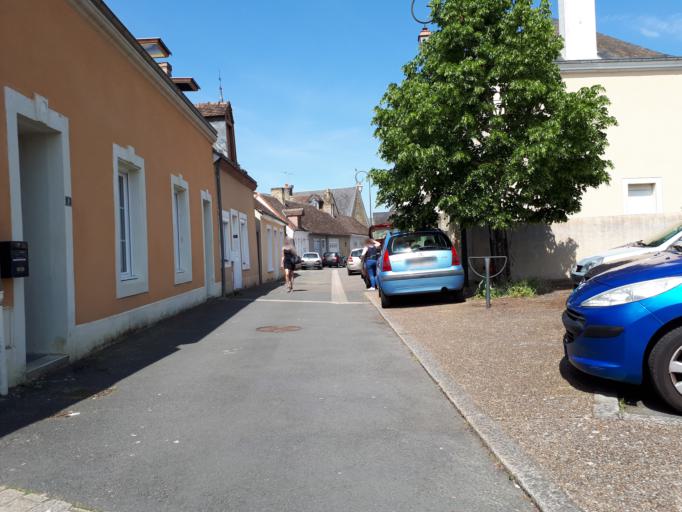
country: FR
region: Pays de la Loire
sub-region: Departement de la Sarthe
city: Champagne
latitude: 48.0771
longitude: 0.2981
